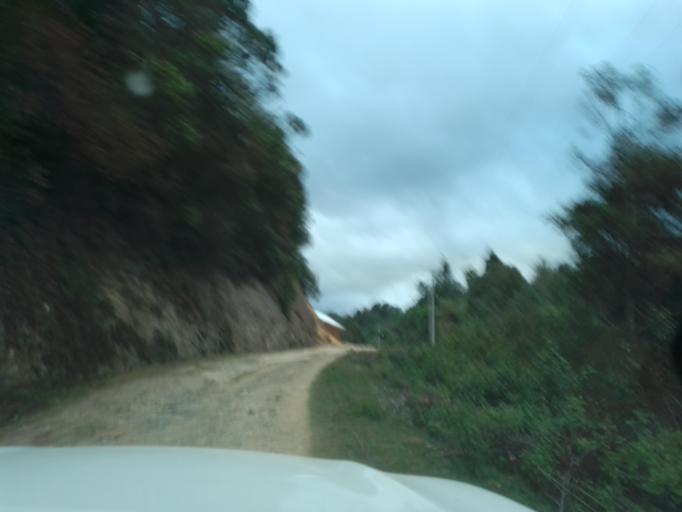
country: MX
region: Chiapas
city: Motozintla de Mendoza
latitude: 15.2138
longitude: -92.2280
